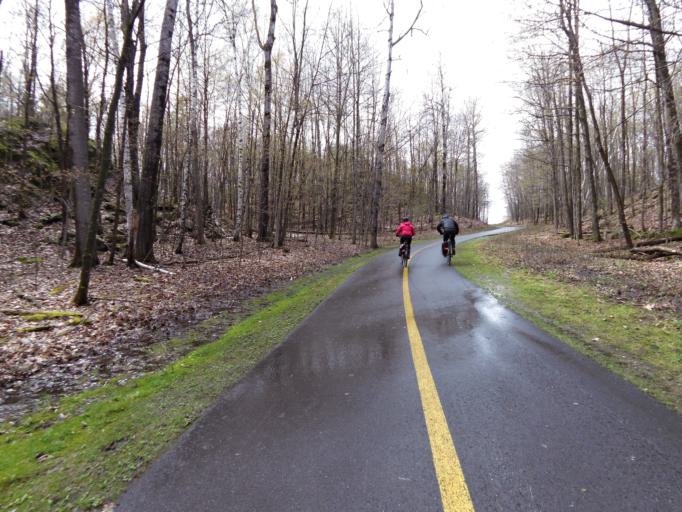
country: CA
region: Quebec
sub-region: Outaouais
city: Gatineau
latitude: 45.4647
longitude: -75.7815
